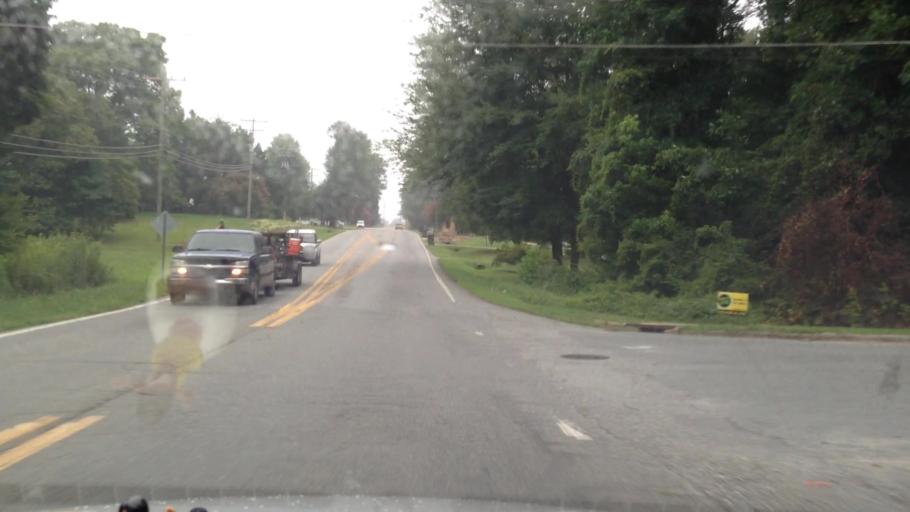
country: US
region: North Carolina
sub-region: Forsyth County
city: Kernersville
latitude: 36.1319
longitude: -80.0711
